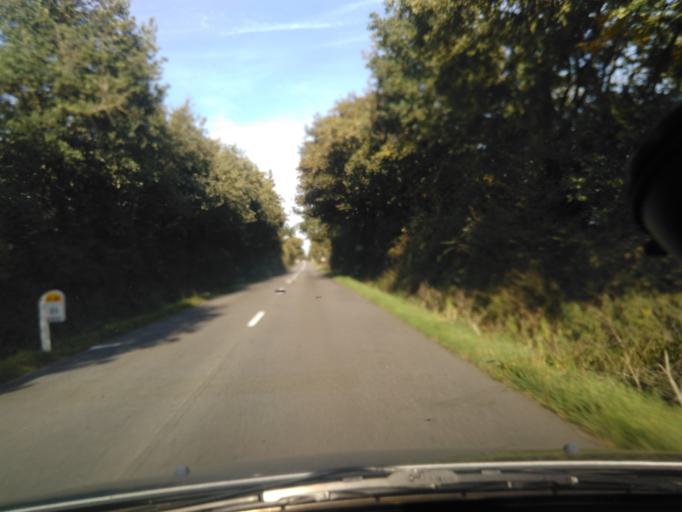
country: FR
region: Pays de la Loire
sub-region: Departement de la Vendee
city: Nieul-le-Dolent
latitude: 46.5811
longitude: -1.4895
